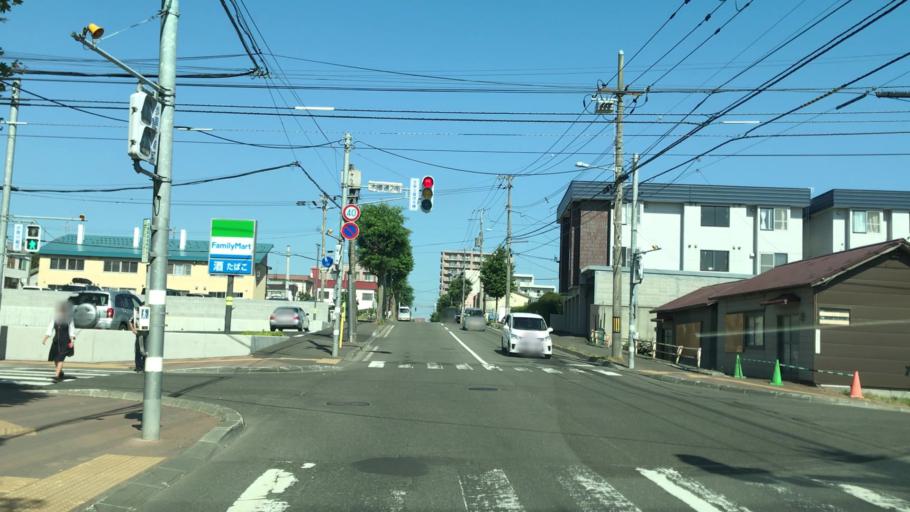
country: JP
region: Hokkaido
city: Sapporo
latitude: 43.0475
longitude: 141.4045
